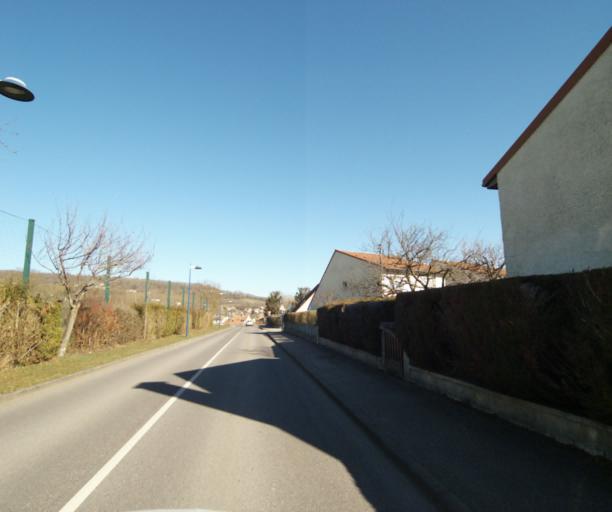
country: FR
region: Lorraine
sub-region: Departement de Meurthe-et-Moselle
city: Ludres
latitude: 48.6168
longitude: 6.1658
